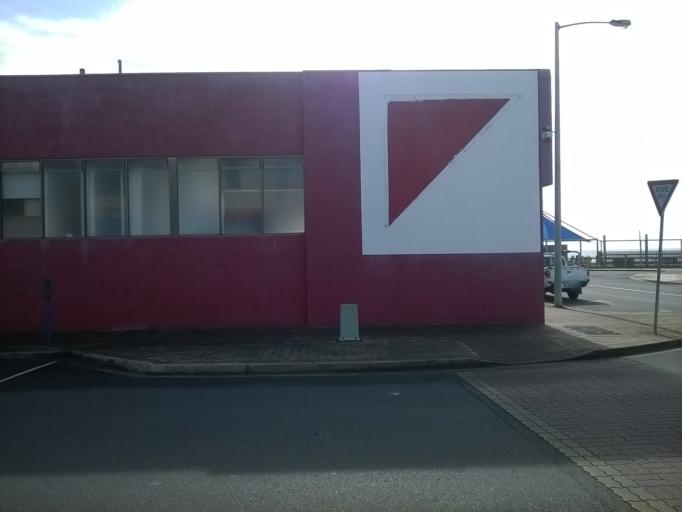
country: AU
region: Tasmania
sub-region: Burnie
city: Burnie
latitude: -41.0495
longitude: 145.9039
